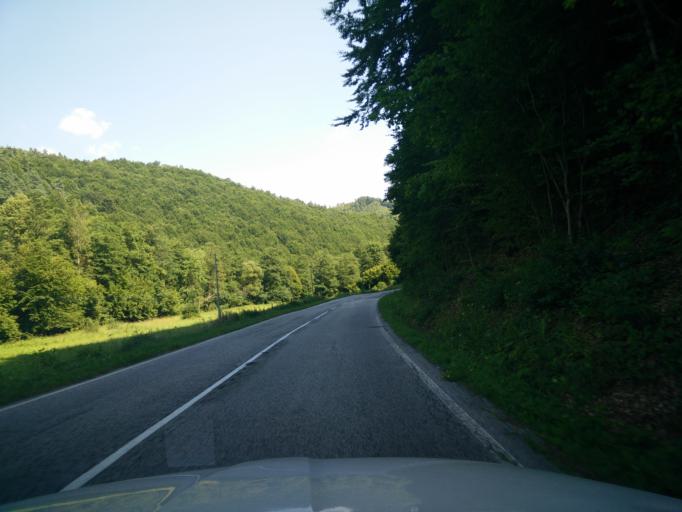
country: SK
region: Nitriansky
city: Bojnice
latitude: 48.8635
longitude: 18.4584
